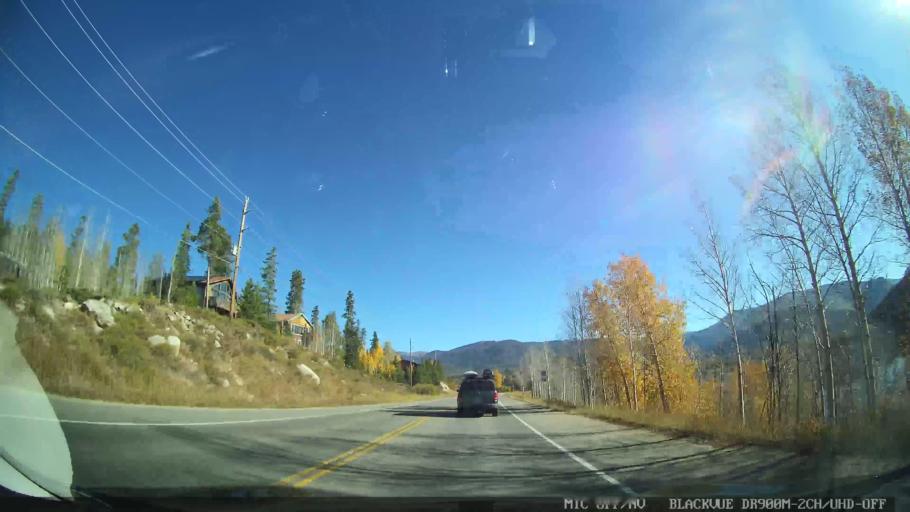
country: US
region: Colorado
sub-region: Grand County
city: Granby
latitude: 40.2397
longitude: -105.8460
